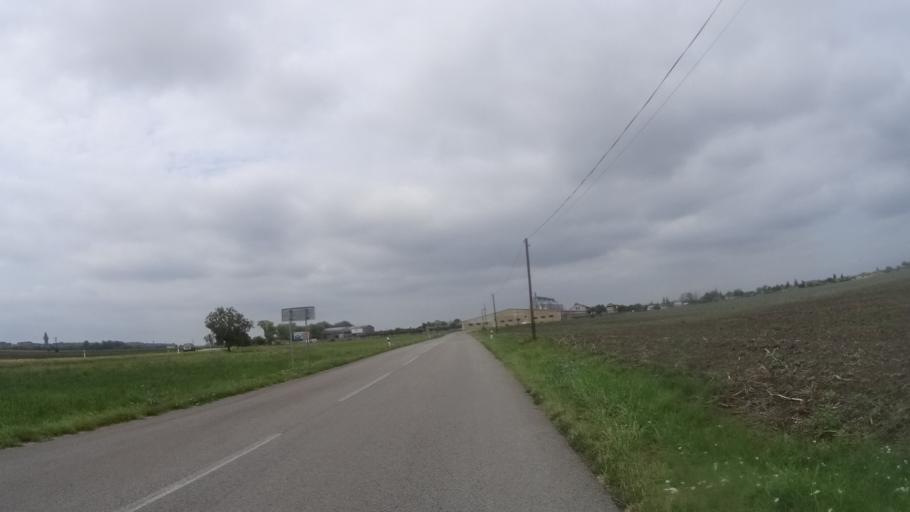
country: HU
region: Komarom-Esztergom
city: Acs
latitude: 47.7665
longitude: 17.9912
